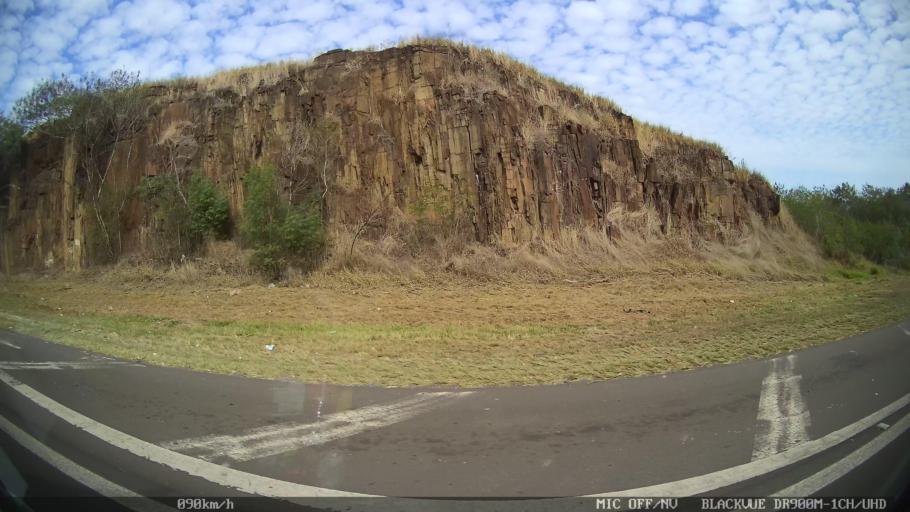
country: BR
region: Sao Paulo
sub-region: Santa Barbara D'Oeste
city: Santa Barbara d'Oeste
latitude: -22.7660
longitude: -47.4089
